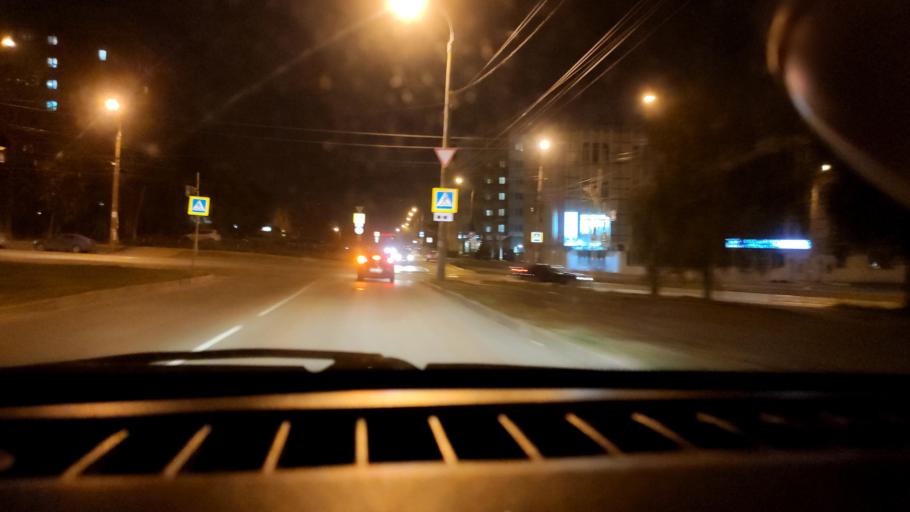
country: RU
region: Samara
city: Samara
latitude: 53.1916
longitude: 50.1720
